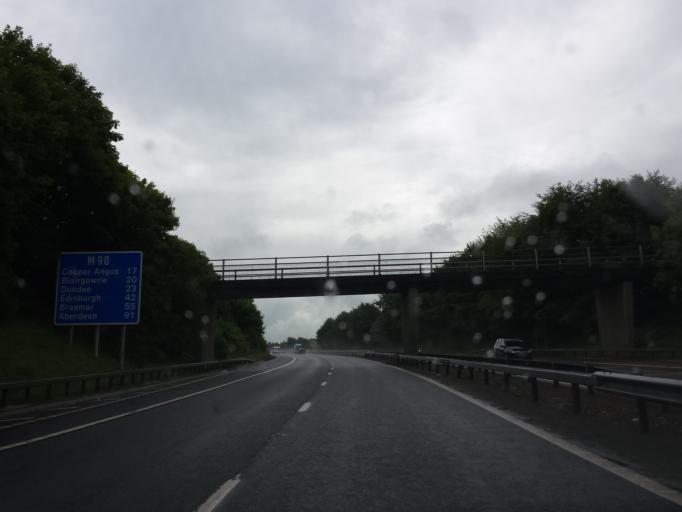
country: GB
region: Scotland
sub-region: Perth and Kinross
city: Perth
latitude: 56.3856
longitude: -3.4806
